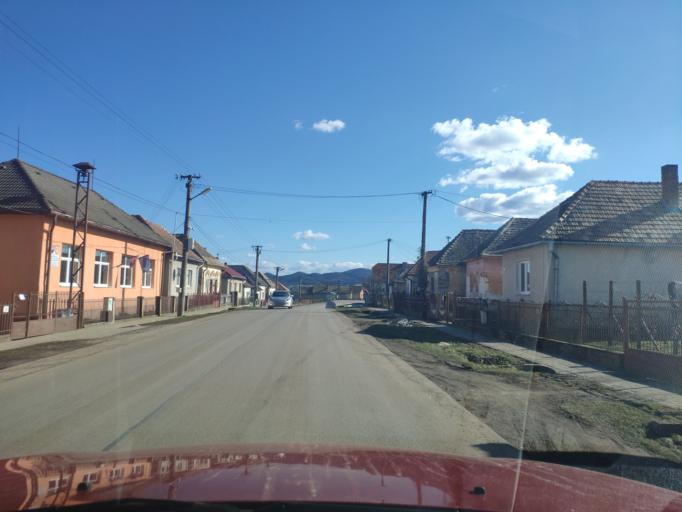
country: SK
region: Banskobystricky
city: Rimavska Sobota
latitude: 48.2874
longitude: 20.0912
